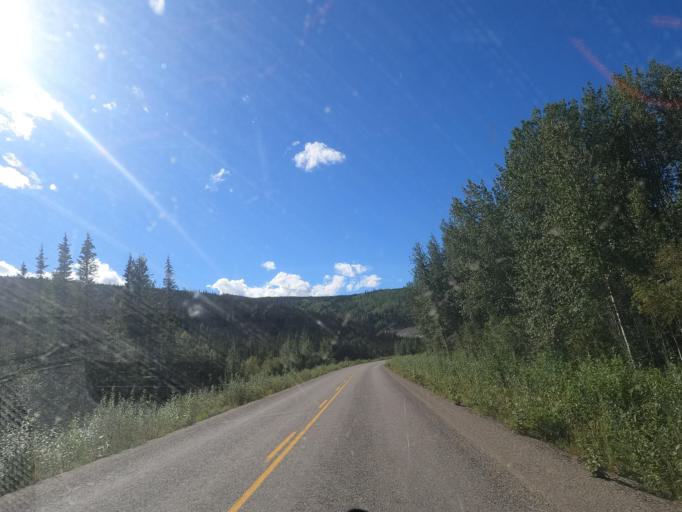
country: CA
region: Yukon
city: Dawson City
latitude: 63.9573
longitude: -138.6971
